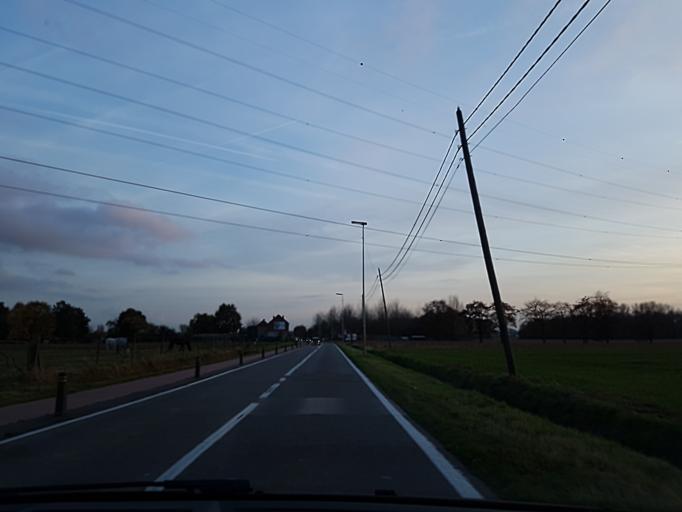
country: BE
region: Flanders
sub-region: Provincie Antwerpen
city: Ranst
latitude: 51.1713
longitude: 4.5635
